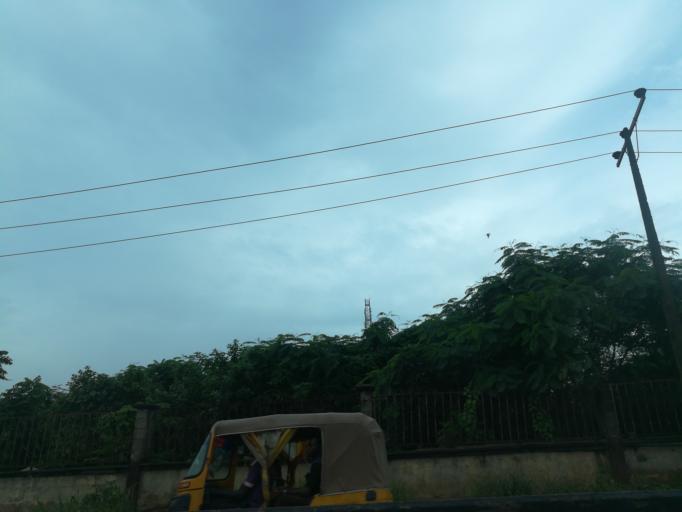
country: NG
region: Lagos
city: Ikorodu
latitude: 6.6272
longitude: 3.5064
